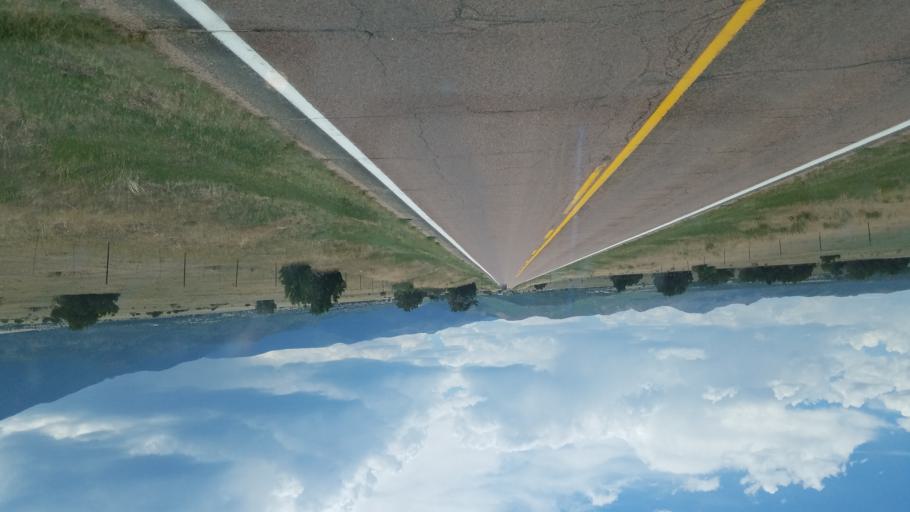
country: US
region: Colorado
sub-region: Fremont County
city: Florence
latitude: 38.2669
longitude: -105.0875
